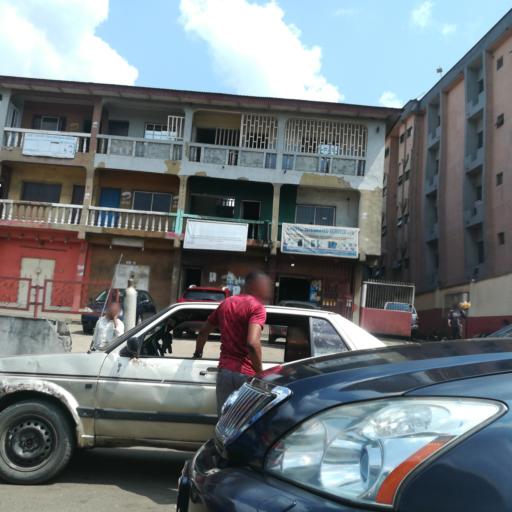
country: NG
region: Rivers
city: Port Harcourt
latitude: 4.8568
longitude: 7.0661
